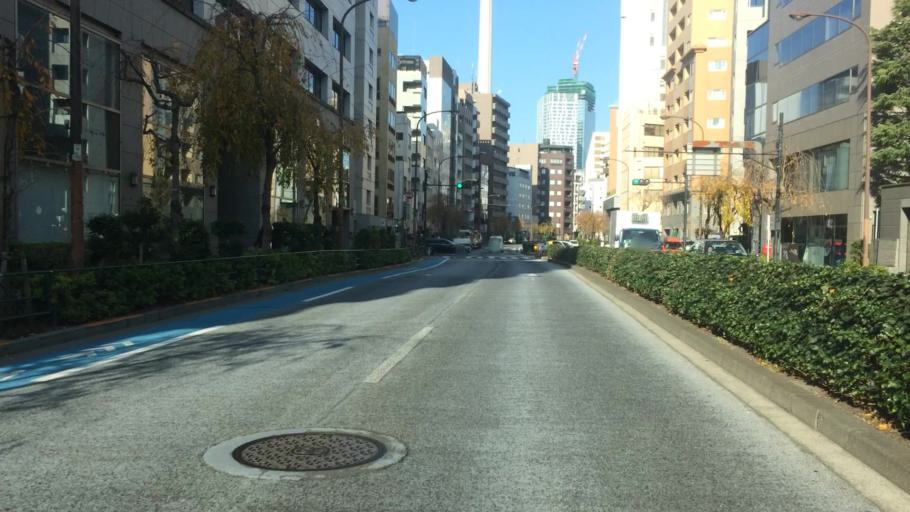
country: JP
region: Tokyo
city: Tokyo
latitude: 35.6494
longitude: 139.7108
